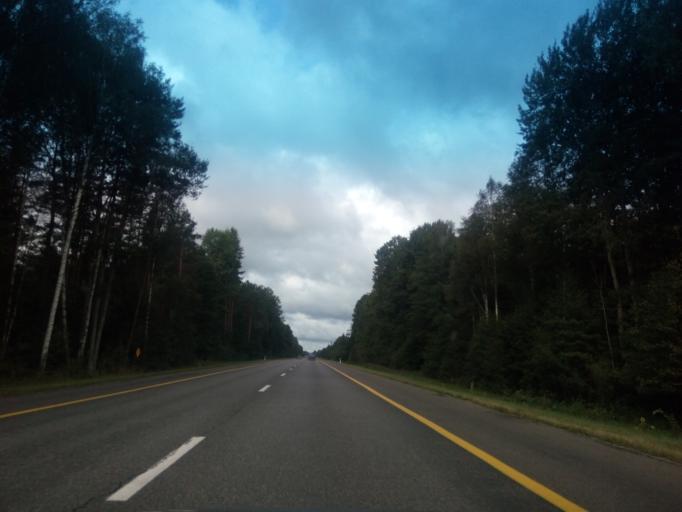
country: BY
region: Vitebsk
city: Lyepyel'
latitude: 54.7695
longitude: 28.4217
